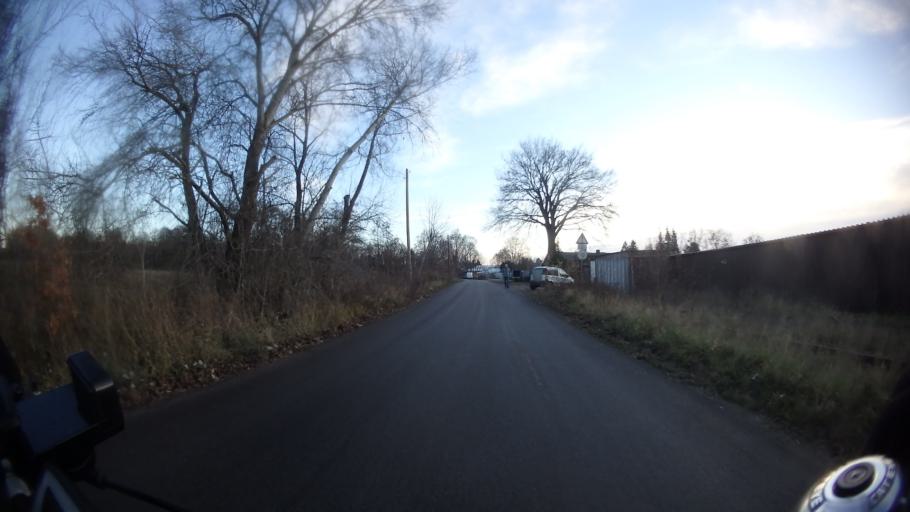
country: DE
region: Schleswig-Holstein
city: Bad Schwartau
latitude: 53.9057
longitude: 10.6960
